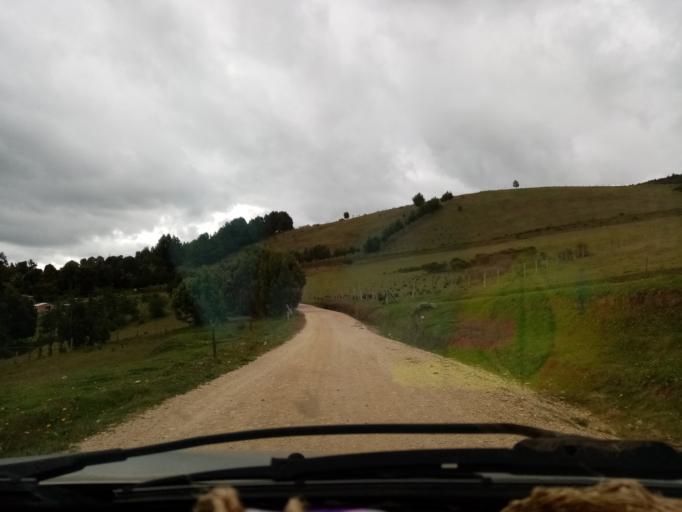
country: CO
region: Boyaca
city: Toca
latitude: 5.6052
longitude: -73.2376
